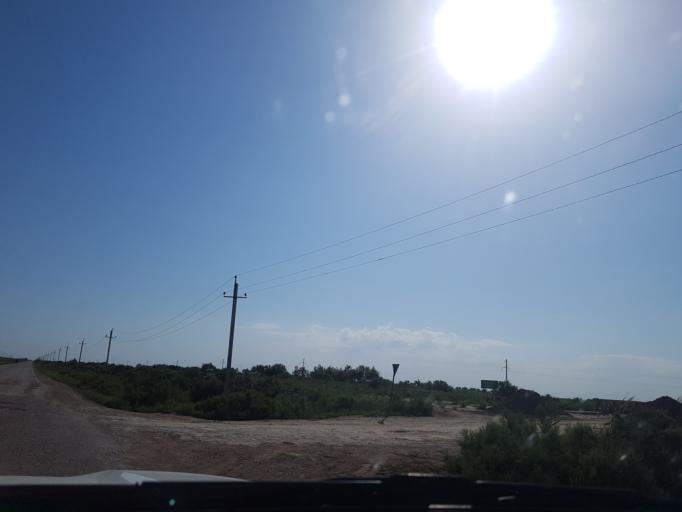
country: TM
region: Dasoguz
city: Koeneuergench
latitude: 42.0790
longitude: 58.8715
